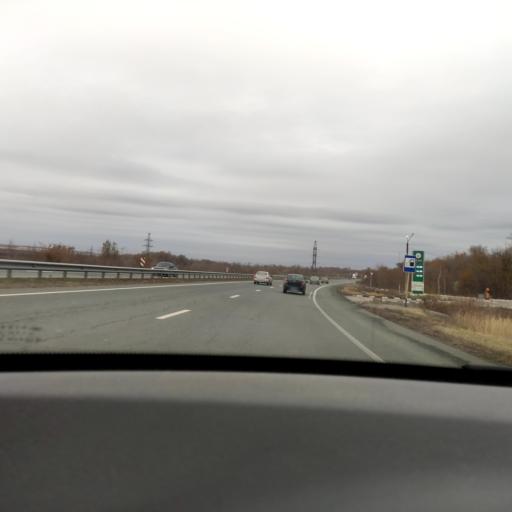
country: RU
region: Samara
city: Novokuybyshevsk
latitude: 53.0227
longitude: 49.9850
